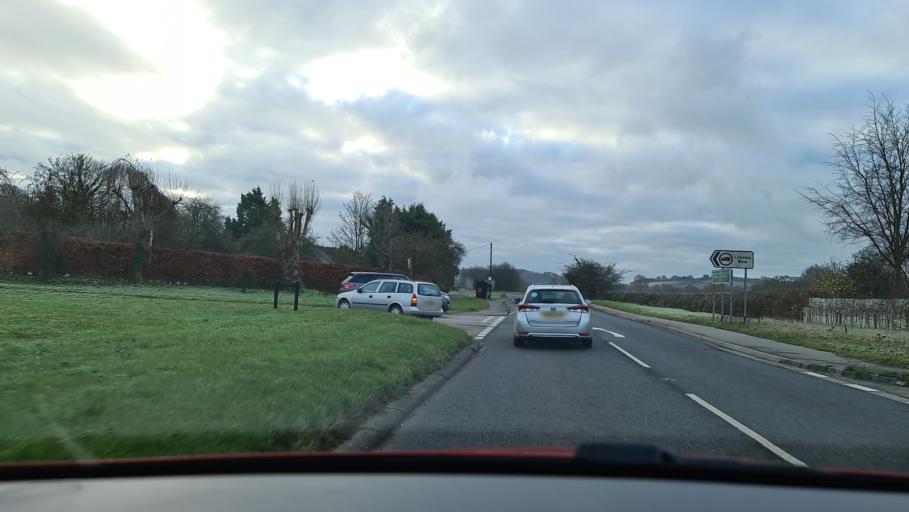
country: GB
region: England
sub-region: Buckinghamshire
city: Princes Risborough
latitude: 51.6896
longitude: -0.8321
